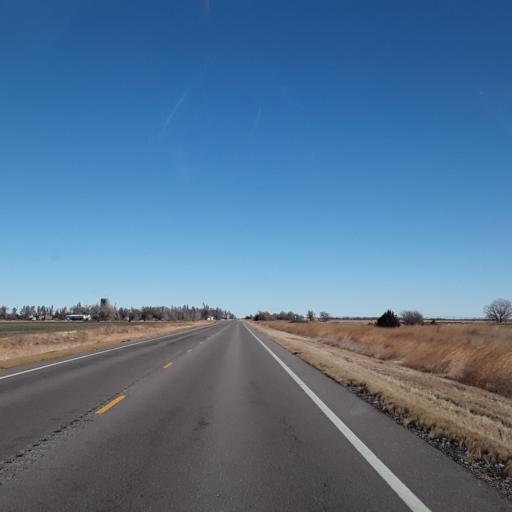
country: US
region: Kansas
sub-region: Pawnee County
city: Larned
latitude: 38.1122
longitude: -99.1904
